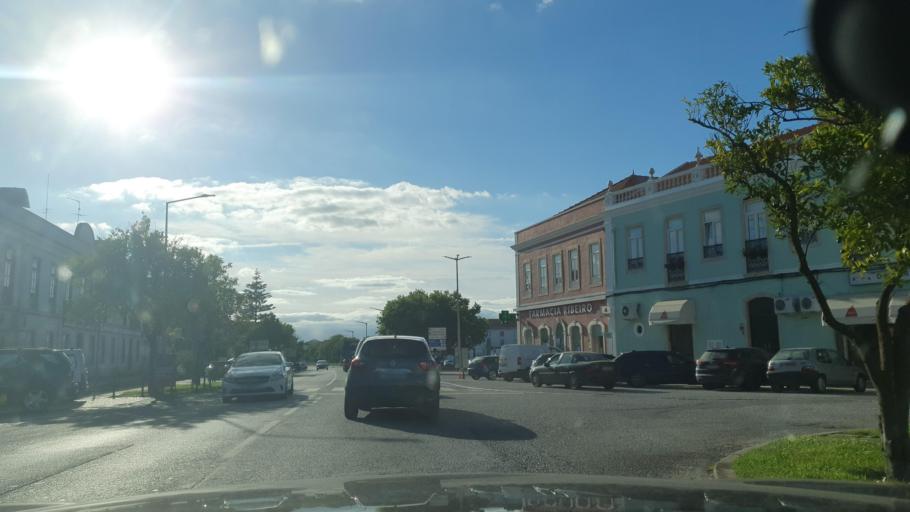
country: PT
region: Evora
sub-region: Vendas Novas
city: Vendas Novas
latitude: 38.6764
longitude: -8.4557
